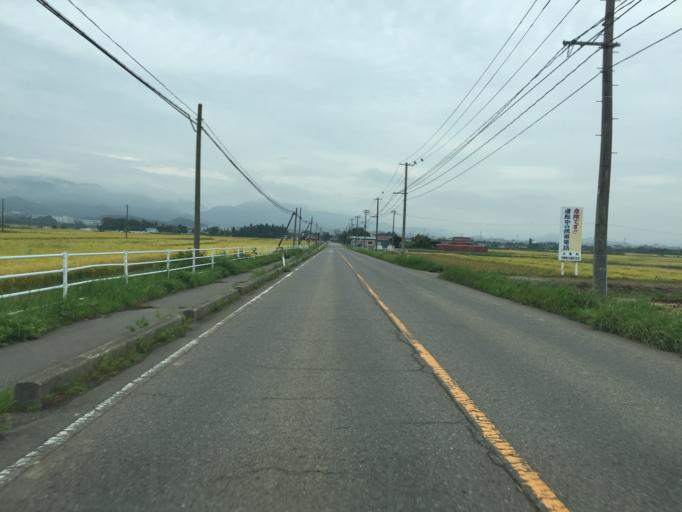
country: JP
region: Fukushima
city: Kitakata
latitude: 37.5419
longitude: 139.9289
